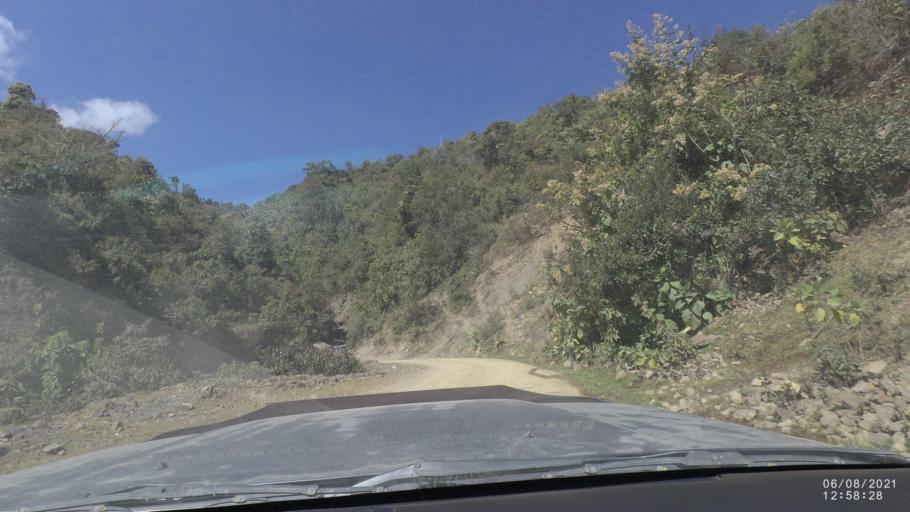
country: BO
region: Cochabamba
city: Colchani
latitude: -16.7513
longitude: -66.6858
